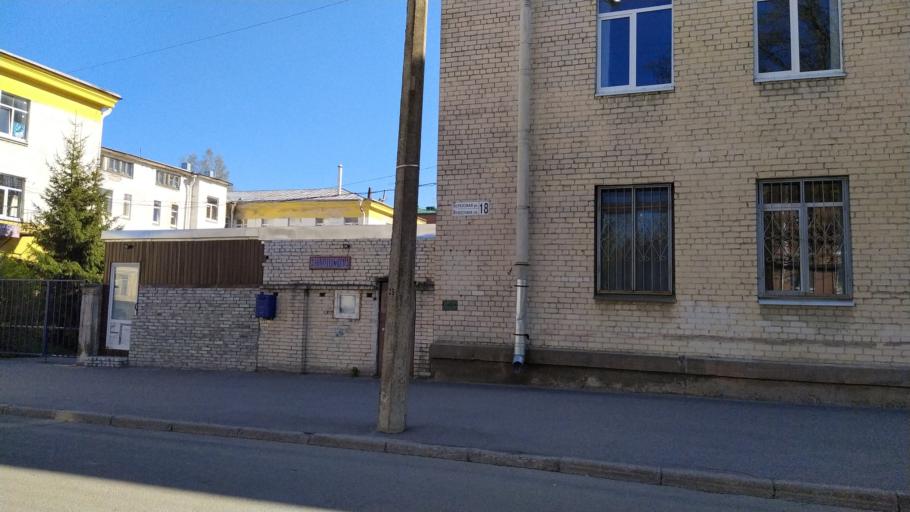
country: RU
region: St.-Petersburg
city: Pavlovsk
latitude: 59.6860
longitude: 30.4282
